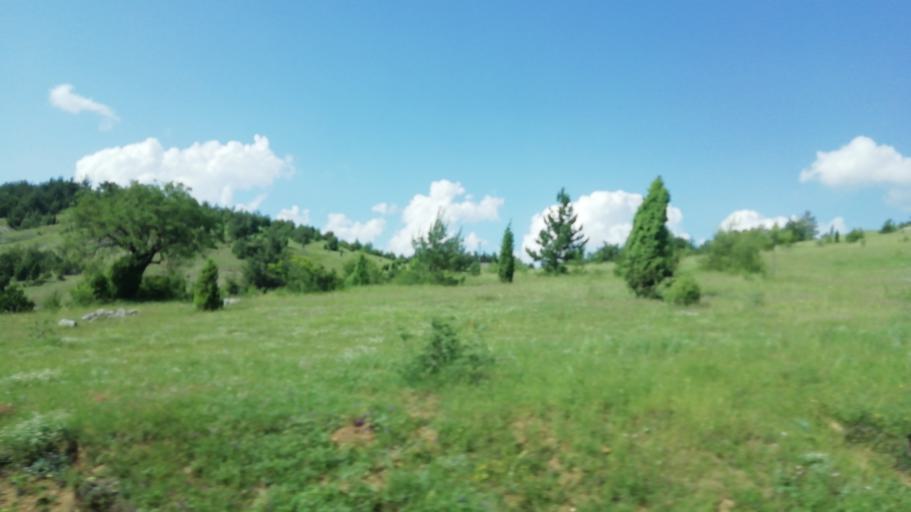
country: TR
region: Karabuk
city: Karabuk
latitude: 41.1302
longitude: 32.5680
